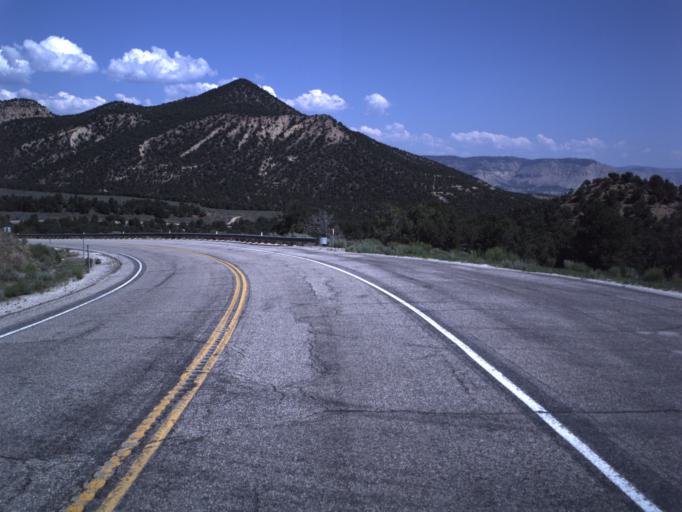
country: US
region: Utah
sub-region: Wayne County
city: Loa
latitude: 38.7225
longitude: -111.3983
